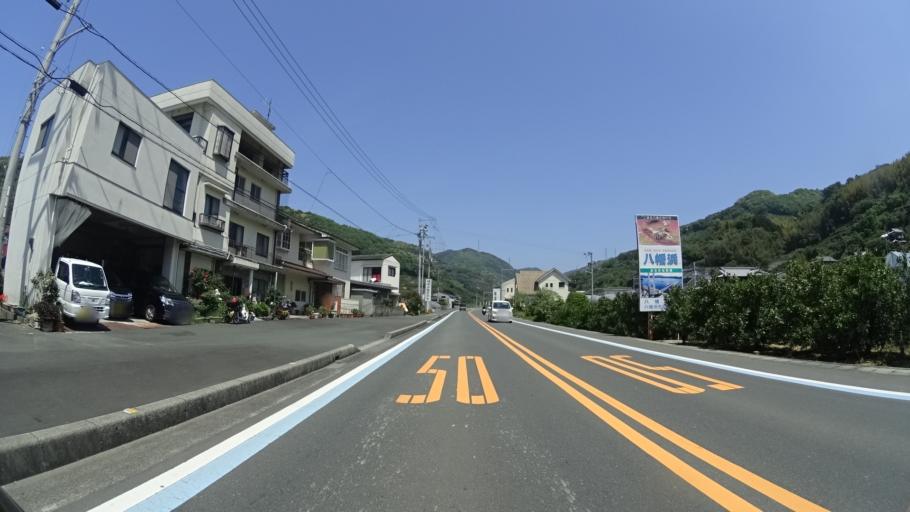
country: JP
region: Ehime
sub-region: Nishiuwa-gun
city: Ikata-cho
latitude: 33.4938
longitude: 132.3972
